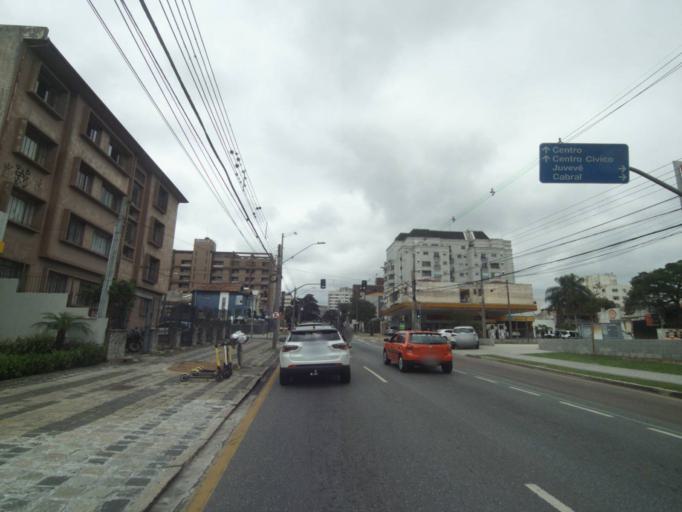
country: BR
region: Parana
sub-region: Curitiba
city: Curitiba
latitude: -25.4268
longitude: -49.2532
